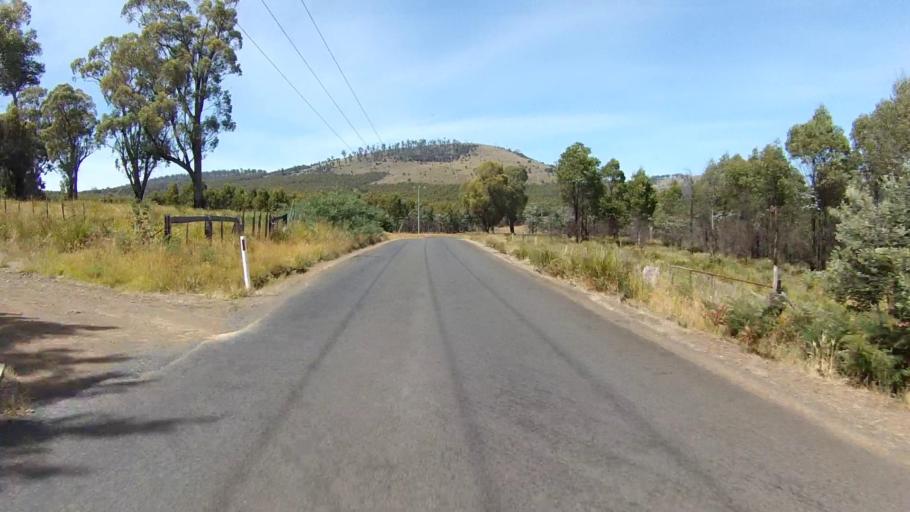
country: AU
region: Tasmania
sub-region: Sorell
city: Sorell
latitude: -42.6178
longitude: 147.7303
